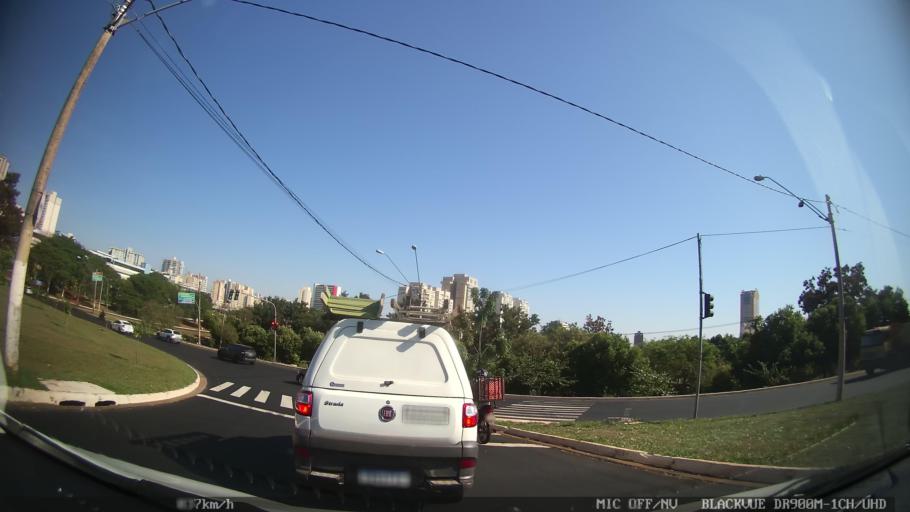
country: BR
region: Sao Paulo
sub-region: Ribeirao Preto
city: Ribeirao Preto
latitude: -21.2172
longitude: -47.8152
